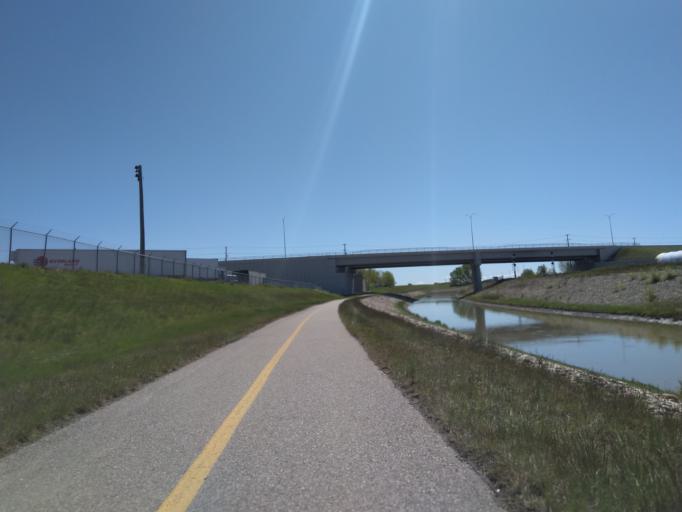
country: CA
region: Alberta
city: Calgary
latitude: 50.9642
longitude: -113.9611
